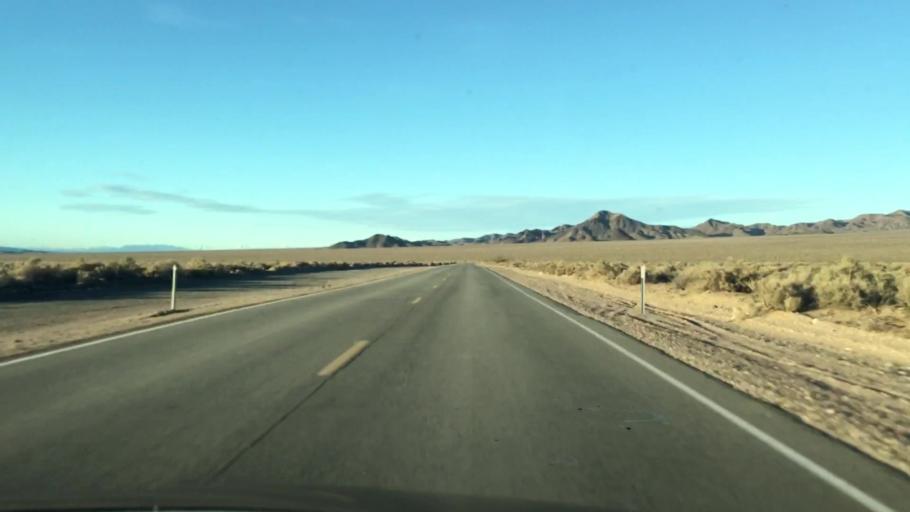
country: US
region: California
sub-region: San Bernardino County
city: Fort Irwin
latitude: 35.3372
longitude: -116.0823
